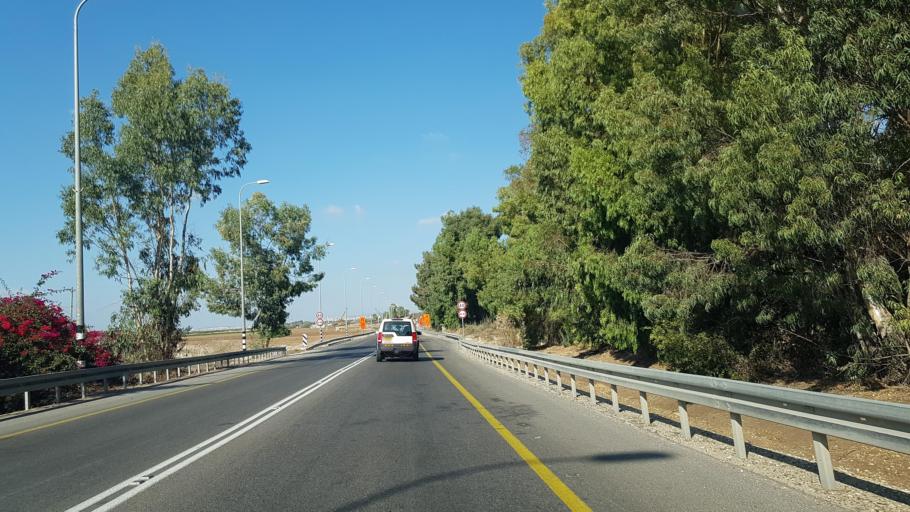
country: PS
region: West Bank
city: Tulkarm
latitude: 32.3307
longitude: 35.0040
